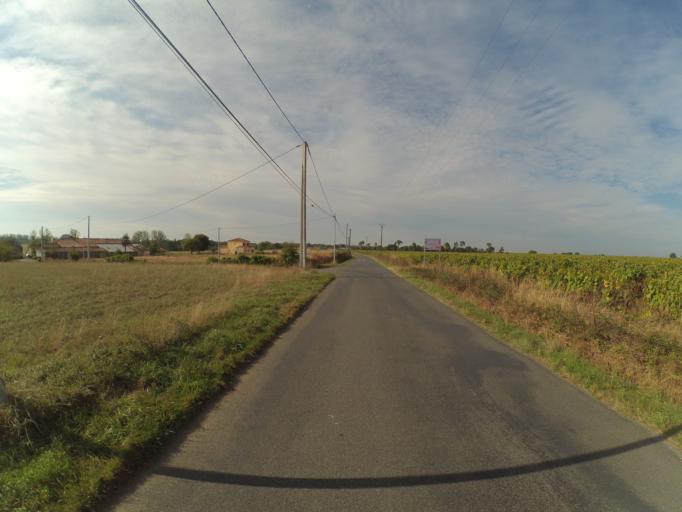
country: FR
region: Pays de la Loire
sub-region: Departement de Maine-et-Loire
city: Tillieres
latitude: 47.1358
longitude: -1.1845
